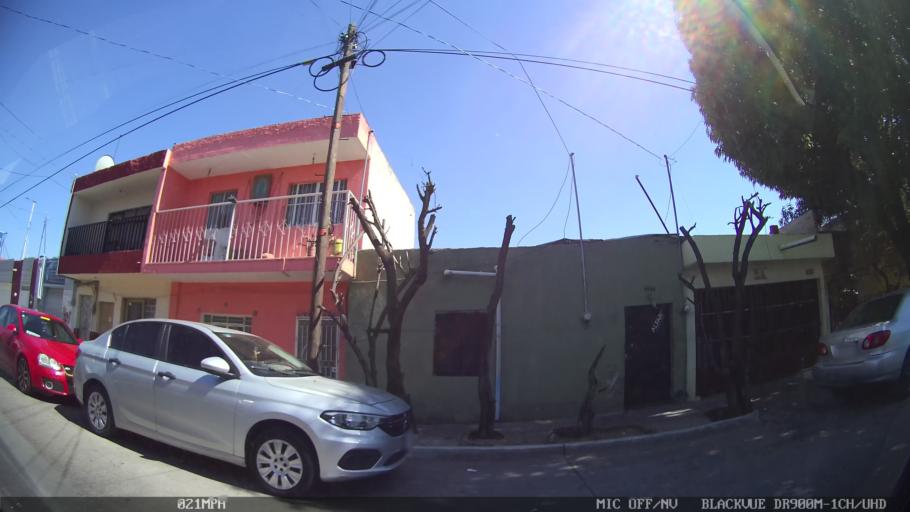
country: MX
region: Jalisco
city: Tlaquepaque
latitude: 20.6546
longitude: -103.2908
